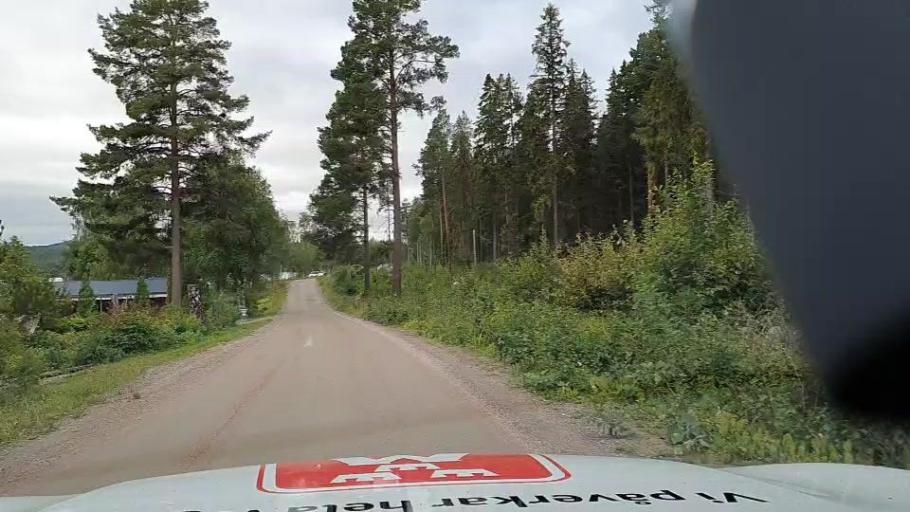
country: SE
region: Jaemtland
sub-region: Ragunda Kommun
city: Hammarstrand
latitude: 63.1685
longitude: 15.8299
